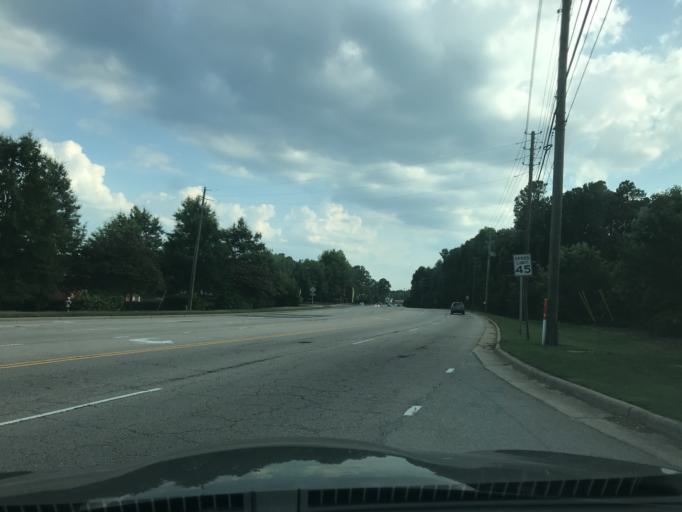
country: US
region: North Carolina
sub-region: Wake County
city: Wake Forest
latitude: 35.9072
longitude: -78.6016
